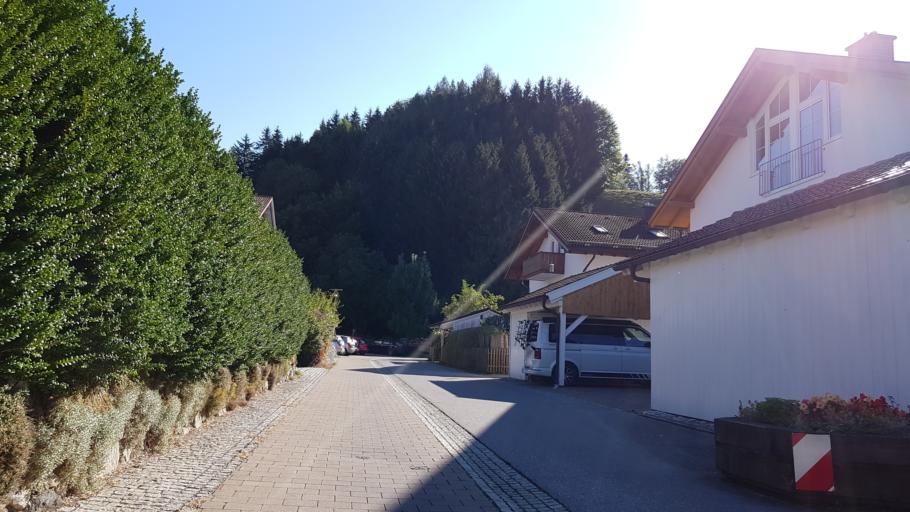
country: DE
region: Bavaria
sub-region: Swabia
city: Fuessen
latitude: 47.5734
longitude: 10.6914
